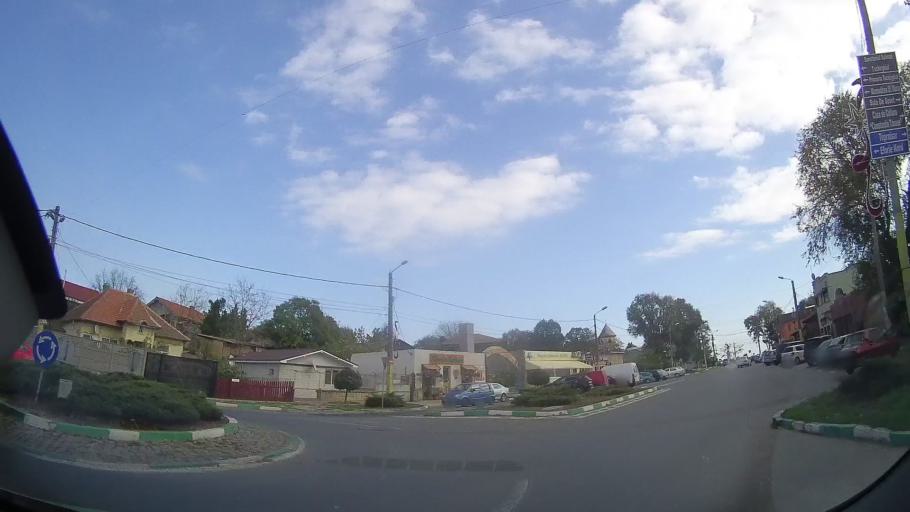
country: RO
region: Constanta
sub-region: Oras Techirghiol
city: Techirghiol
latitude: 44.0553
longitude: 28.6010
